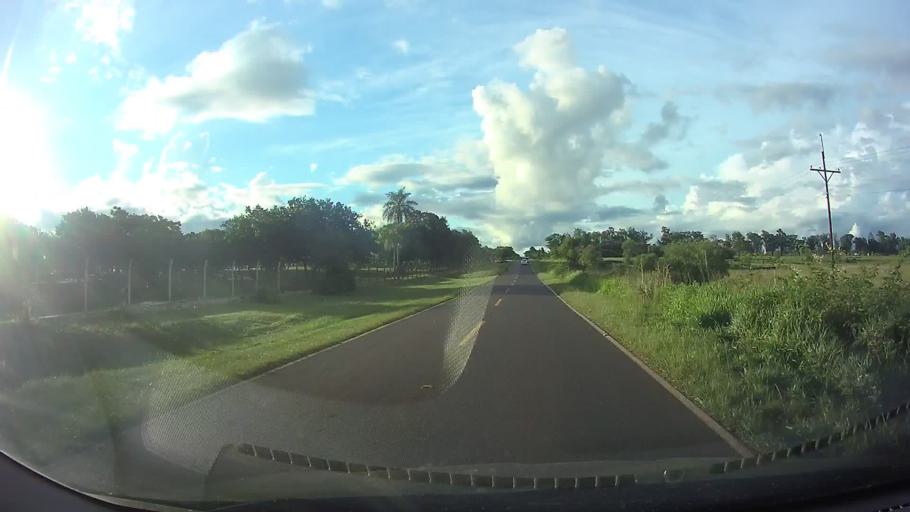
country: PY
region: Paraguari
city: Ybycui
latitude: -25.9979
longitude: -57.0488
